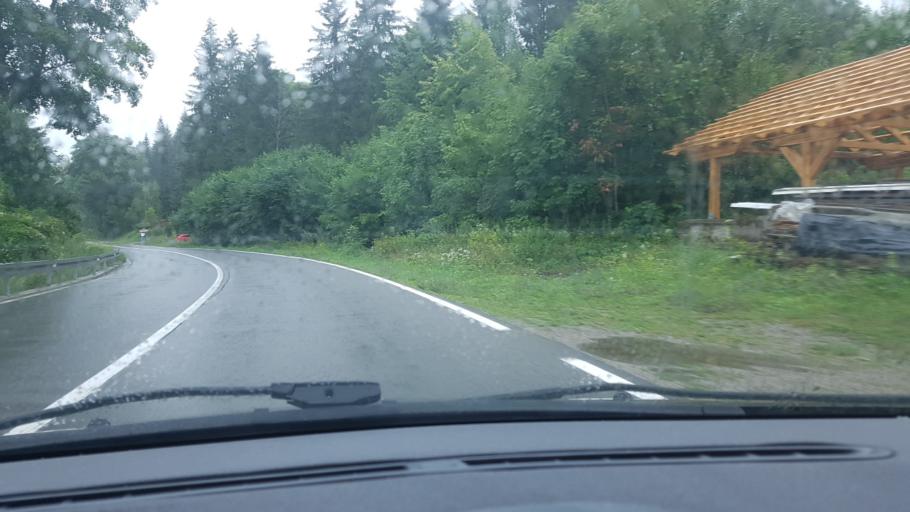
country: HR
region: Primorsko-Goranska
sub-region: Grad Delnice
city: Delnice
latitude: 45.3968
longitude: 14.8991
